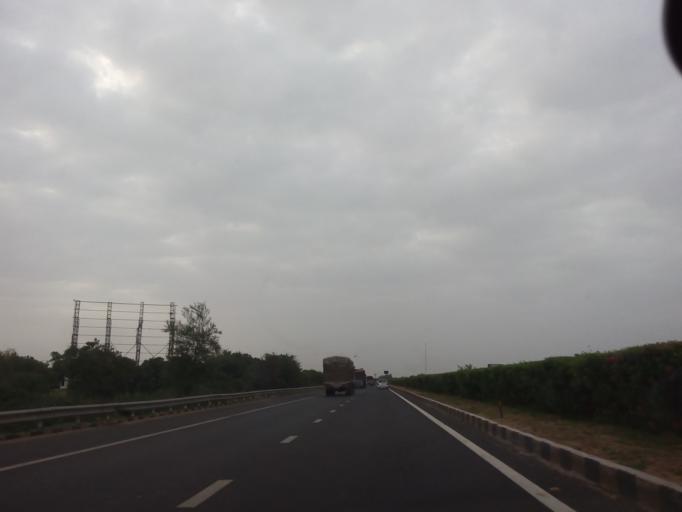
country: IN
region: Gujarat
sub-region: Ahmadabad
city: Ahmedabad
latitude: 22.9670
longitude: 72.6659
